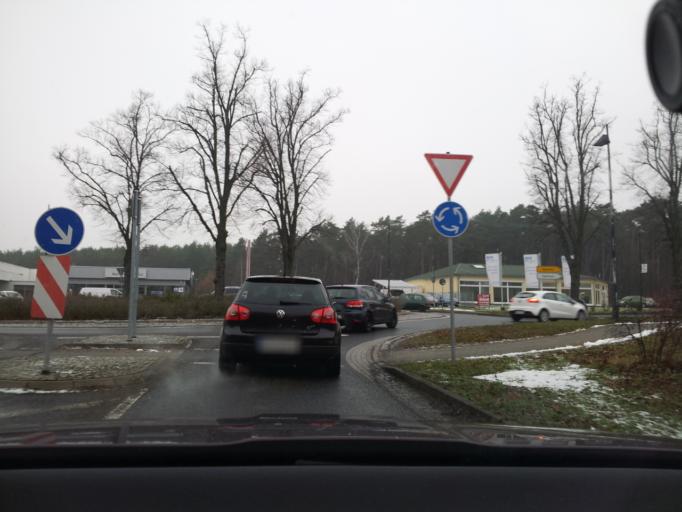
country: DE
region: Brandenburg
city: Wildau
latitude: 52.3179
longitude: 13.6076
